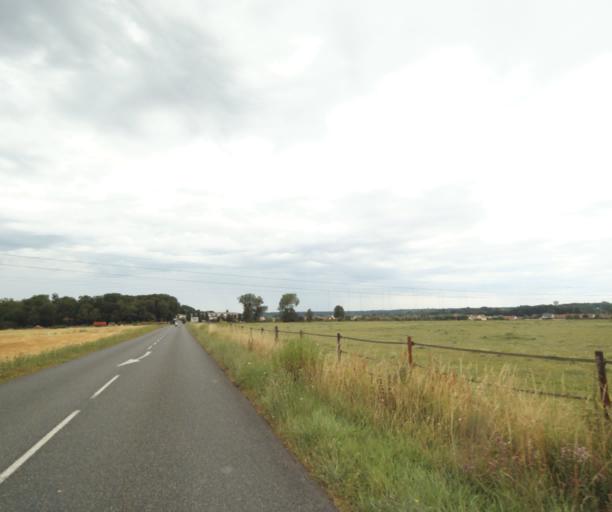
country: FR
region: Ile-de-France
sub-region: Departement de Seine-et-Marne
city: Ponthierry
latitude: 48.5179
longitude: 2.5405
